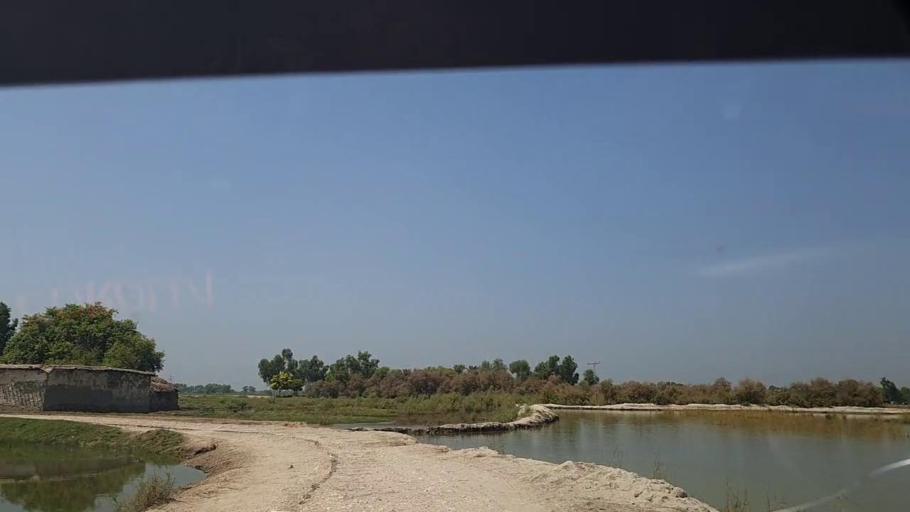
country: PK
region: Sindh
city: Ghauspur
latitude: 28.1871
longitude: 69.0944
